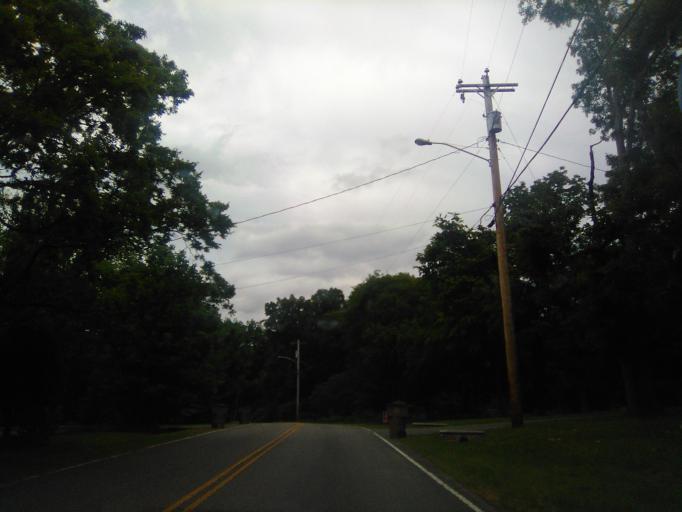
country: US
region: Tennessee
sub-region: Davidson County
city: Belle Meade
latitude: 36.1216
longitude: -86.8824
